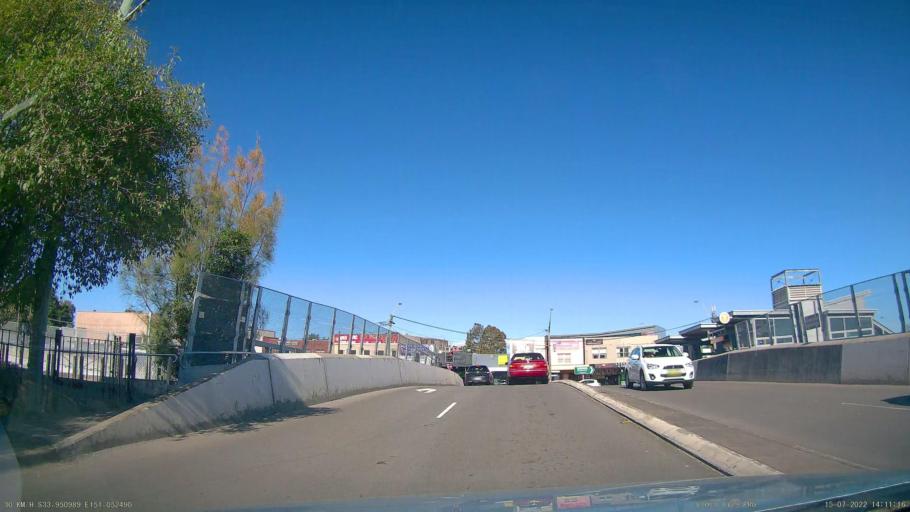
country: AU
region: New South Wales
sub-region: Hurstville
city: Peakhurst
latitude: -33.9511
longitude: 151.0525
